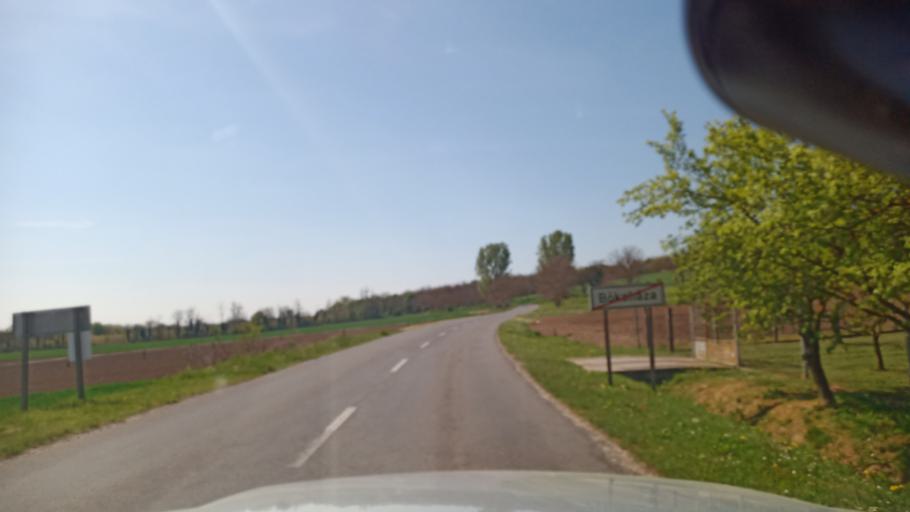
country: HU
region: Zala
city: Heviz
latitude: 46.7701
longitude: 17.1058
